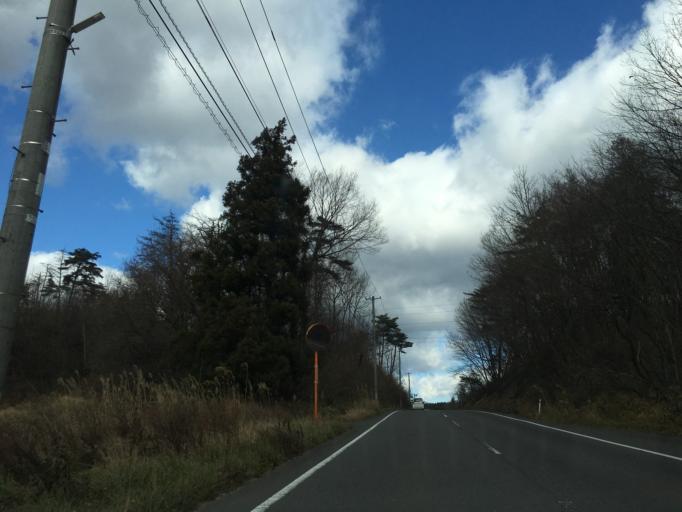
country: JP
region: Fukushima
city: Koriyama
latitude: 37.3531
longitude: 140.4464
